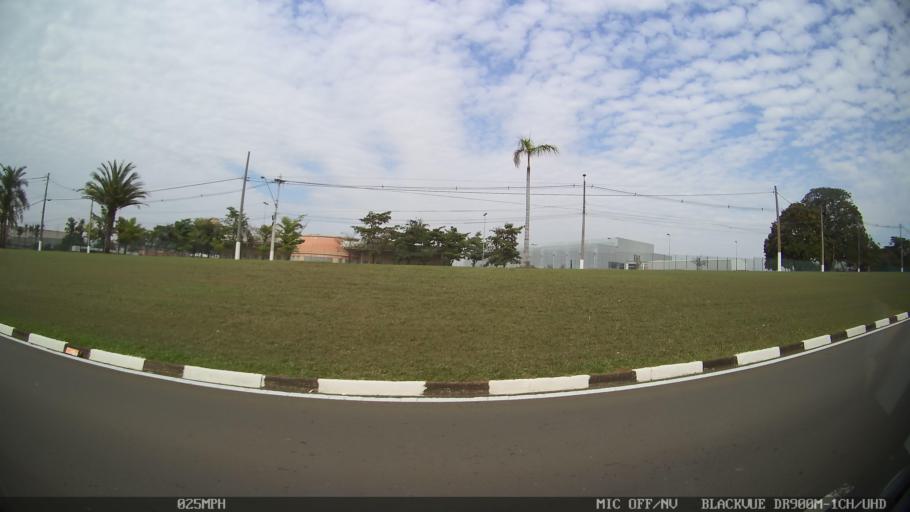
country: BR
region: Sao Paulo
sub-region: Paulinia
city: Paulinia
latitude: -22.7812
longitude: -47.1561
